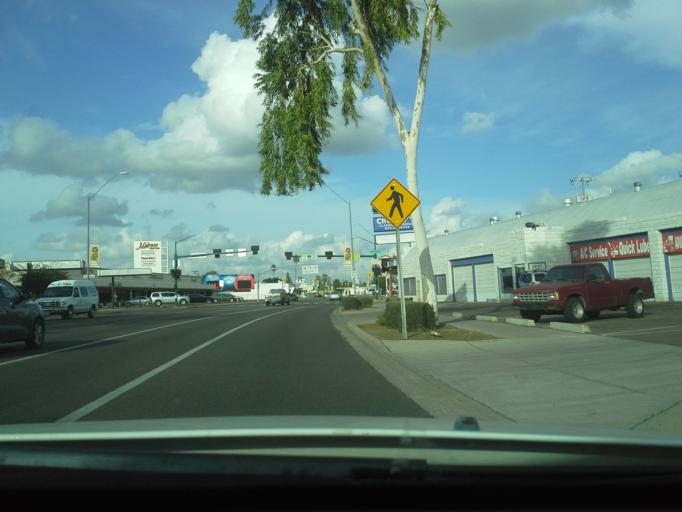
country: US
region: Arizona
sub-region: Maricopa County
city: Phoenix
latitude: 33.4978
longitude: -112.0834
